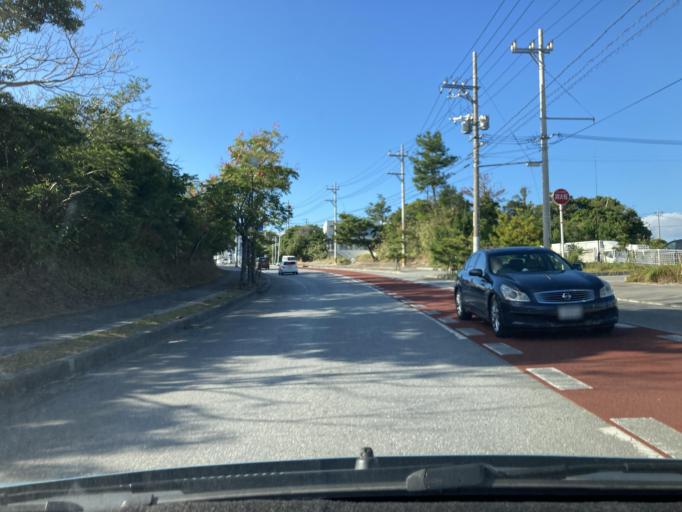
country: JP
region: Okinawa
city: Gushikawa
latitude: 26.3725
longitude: 127.8282
